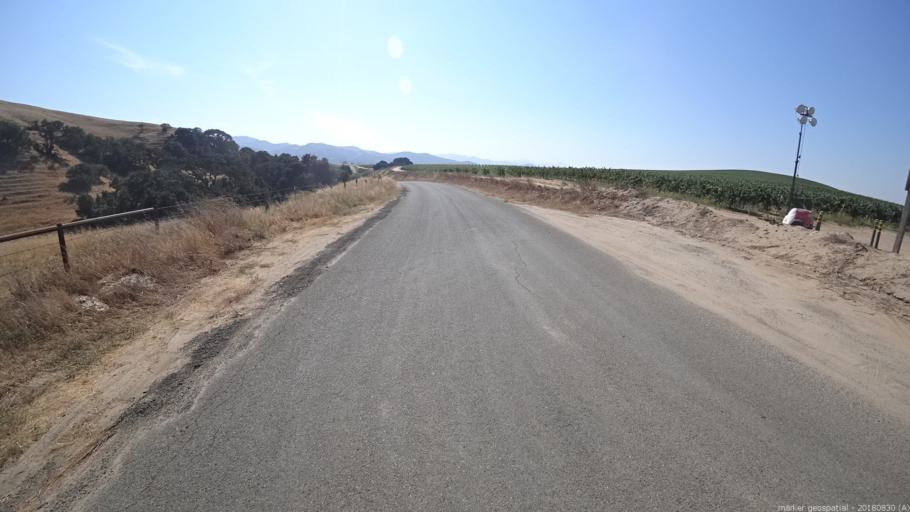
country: US
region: California
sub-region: Monterey County
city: King City
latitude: 36.1129
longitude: -121.0651
